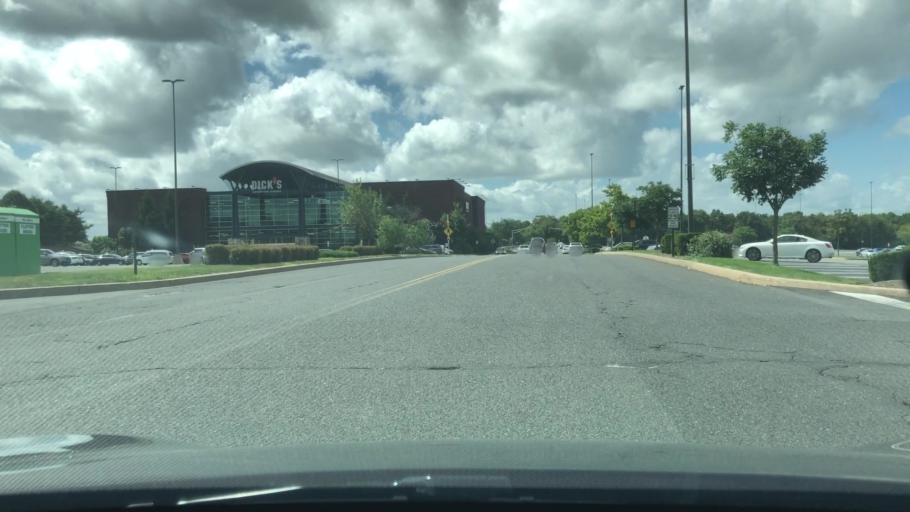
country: US
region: New Jersey
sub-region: Monmouth County
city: West Freehold
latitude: 40.2535
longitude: -74.2971
